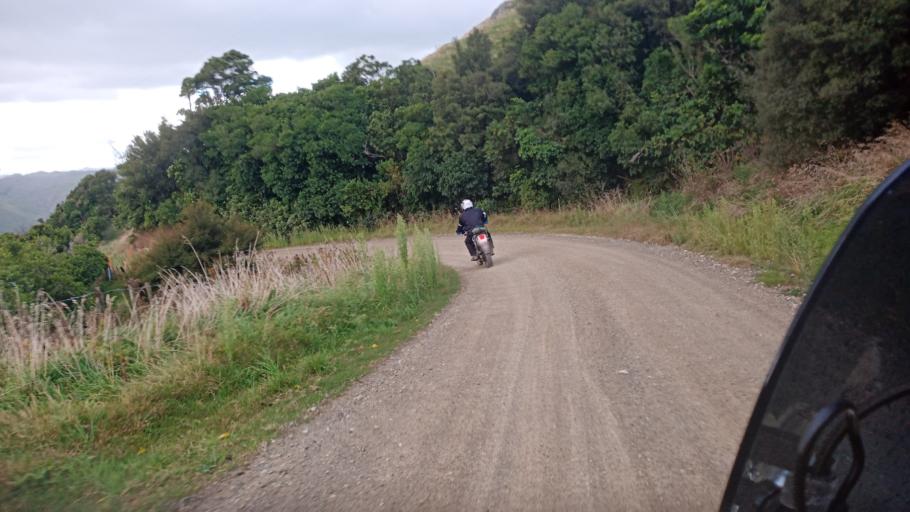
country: NZ
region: Gisborne
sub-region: Gisborne District
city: Gisborne
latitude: -38.4681
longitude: 177.6199
